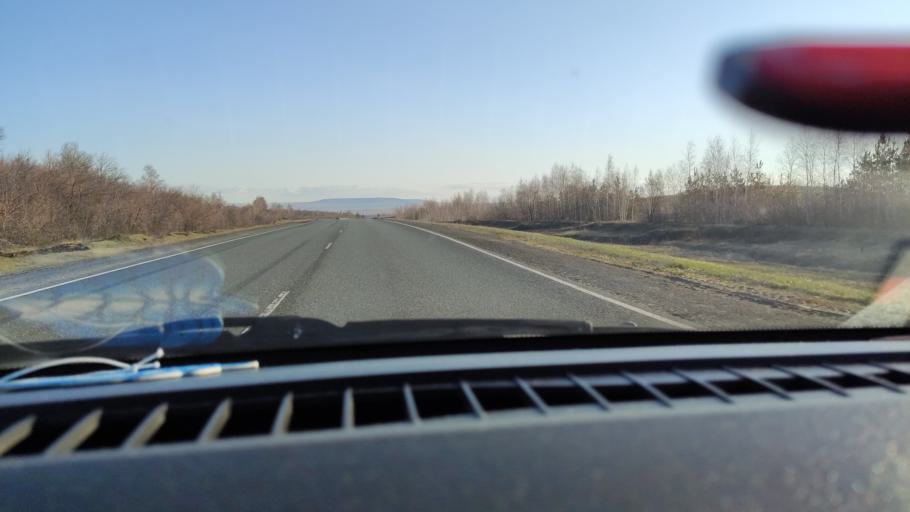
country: RU
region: Saratov
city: Balakovo
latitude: 52.1635
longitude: 47.8243
